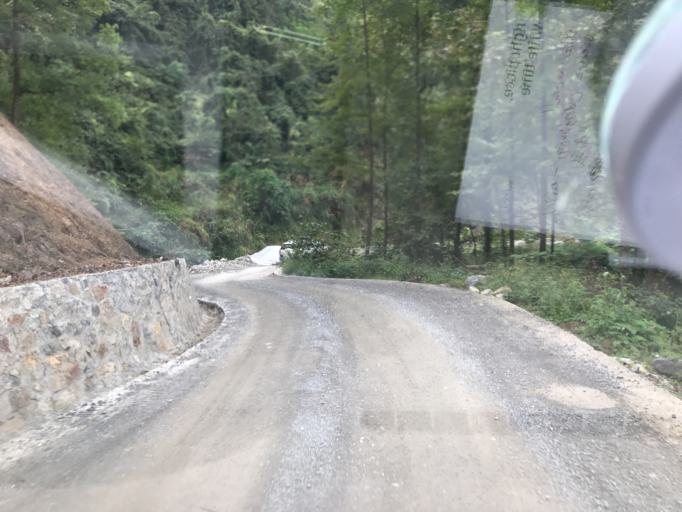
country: CN
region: Guizhou Sheng
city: Donghua
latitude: 28.0593
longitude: 108.1009
